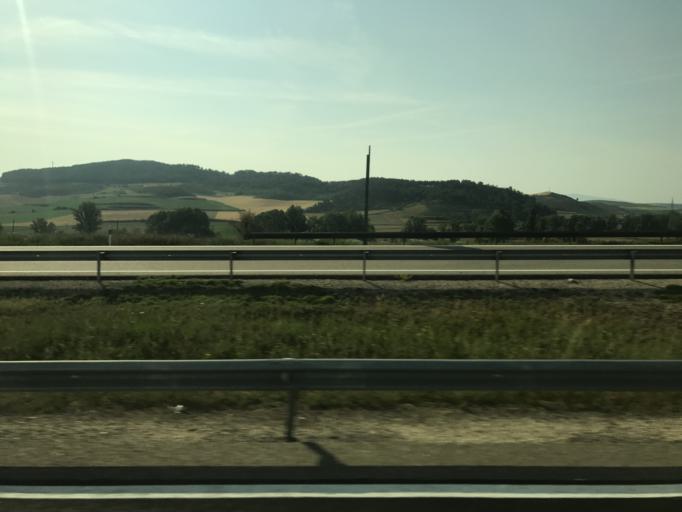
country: ES
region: Castille and Leon
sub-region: Provincia de Burgos
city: Monasterio de Rodilla
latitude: 42.4598
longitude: -3.4518
